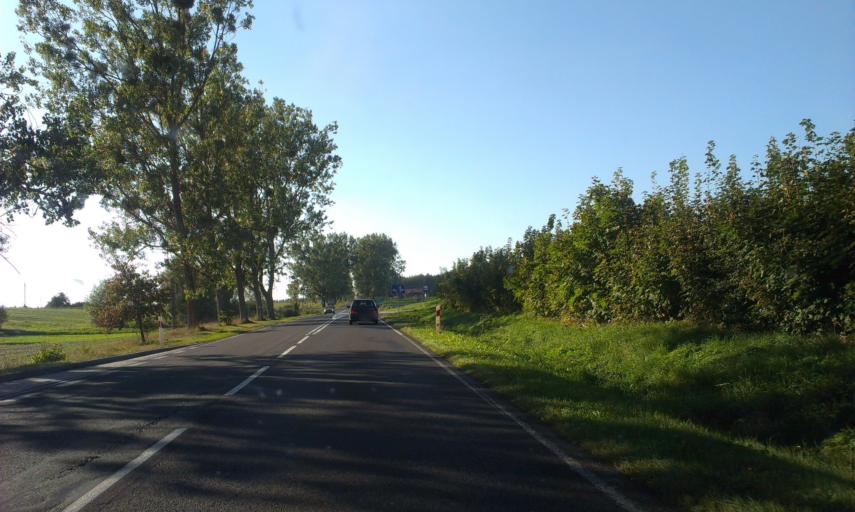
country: PL
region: Kujawsko-Pomorskie
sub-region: Powiat swiecki
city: Bukowiec
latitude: 53.4382
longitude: 18.2882
